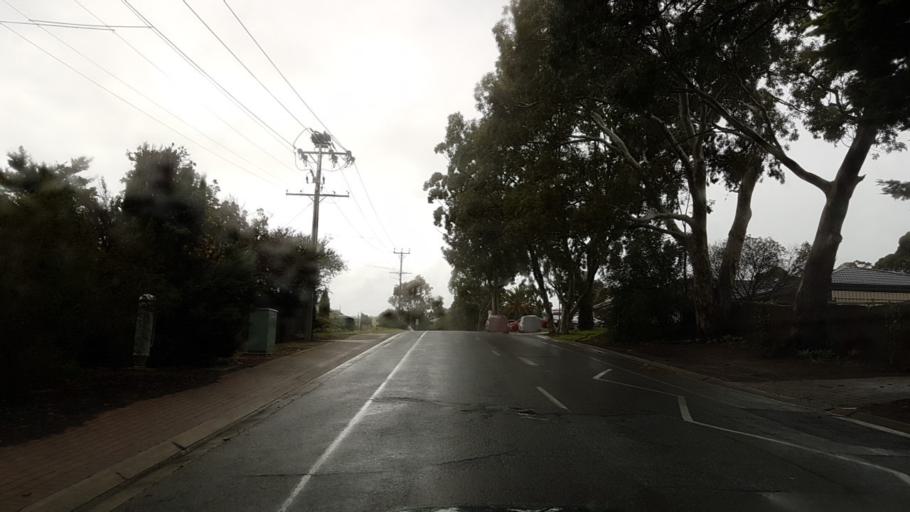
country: AU
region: South Australia
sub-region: Marion
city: Trott Park
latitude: -35.0811
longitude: 138.5846
